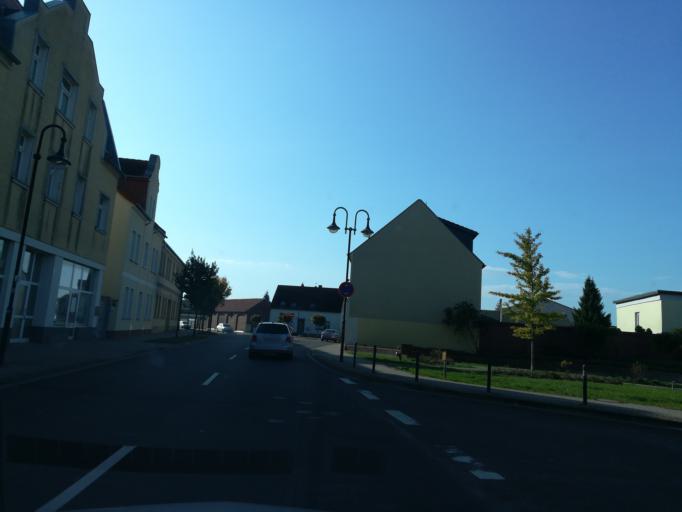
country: DE
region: Saxony-Anhalt
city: Gommern
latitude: 52.0715
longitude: 11.8221
